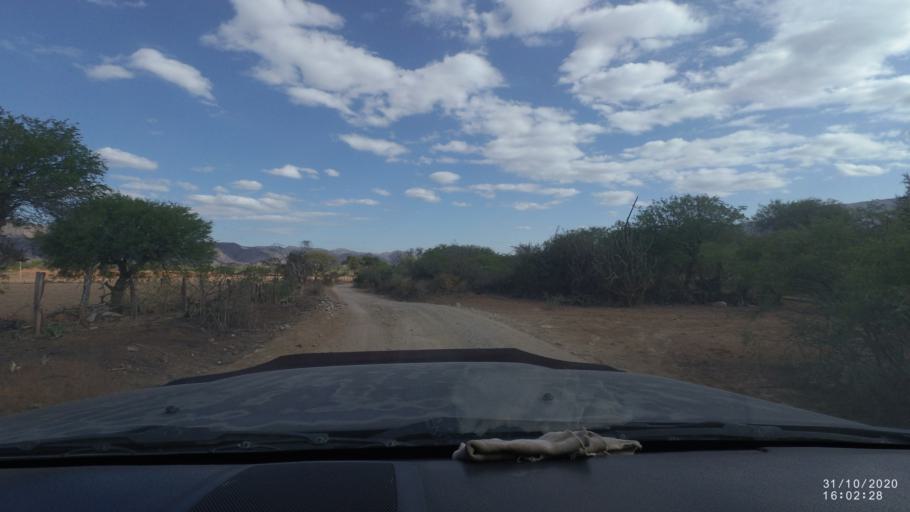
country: BO
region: Chuquisaca
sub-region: Provincia Zudanez
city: Mojocoya
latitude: -18.3472
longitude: -64.6570
